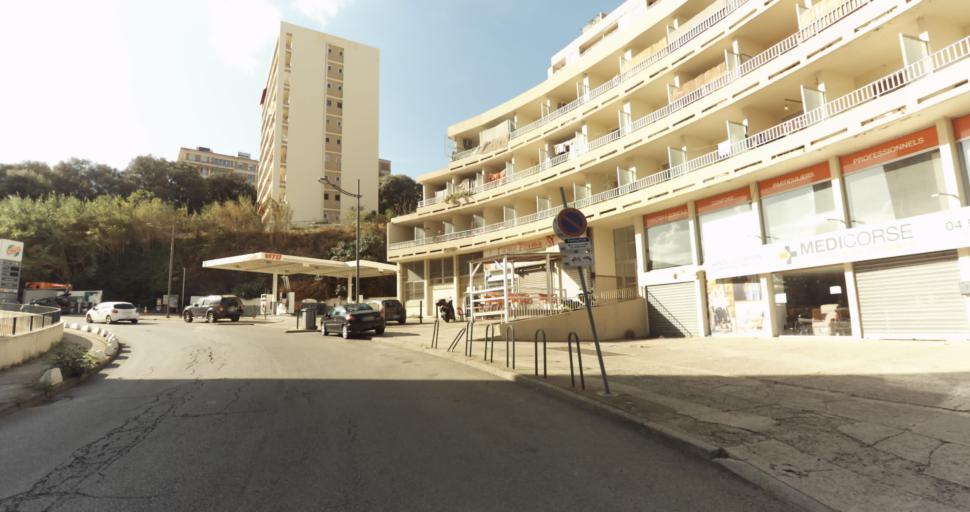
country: FR
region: Corsica
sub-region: Departement de la Corse-du-Sud
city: Ajaccio
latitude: 41.9248
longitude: 8.7342
